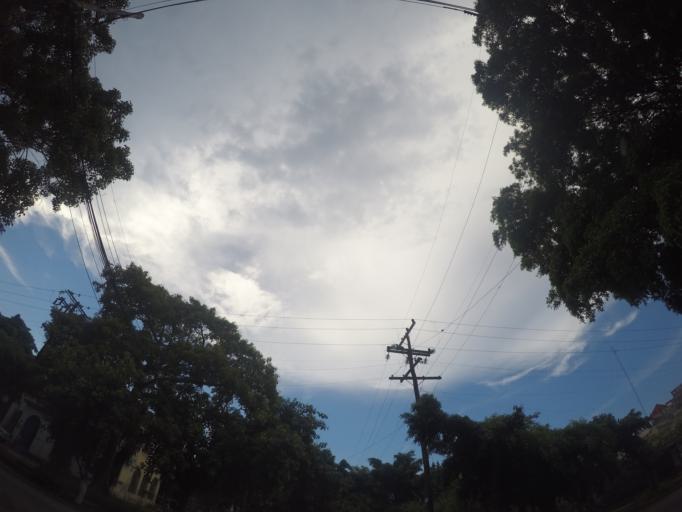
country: CU
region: La Habana
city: Havana
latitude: 23.1183
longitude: -82.4223
